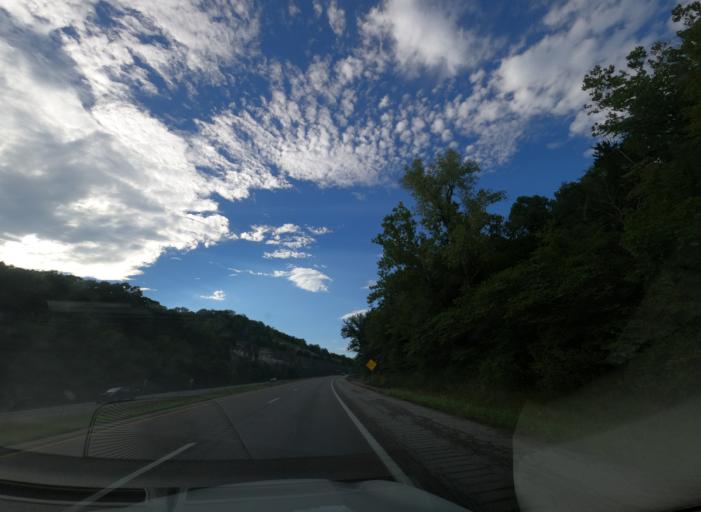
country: US
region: Missouri
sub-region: Jefferson County
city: Crystal City
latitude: 38.1504
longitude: -90.3521
